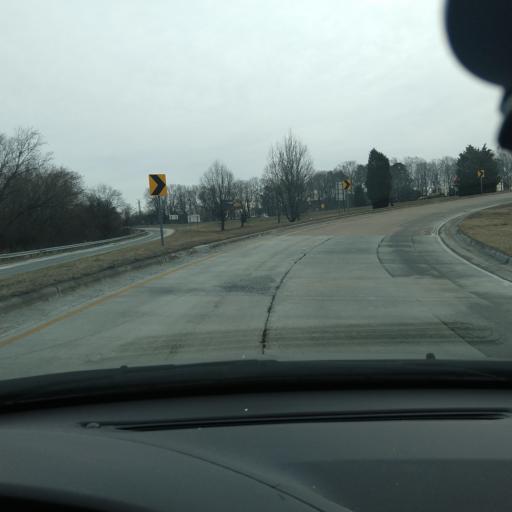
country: US
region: North Carolina
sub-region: Forsyth County
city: Winston-Salem
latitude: 36.0643
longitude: -80.2320
